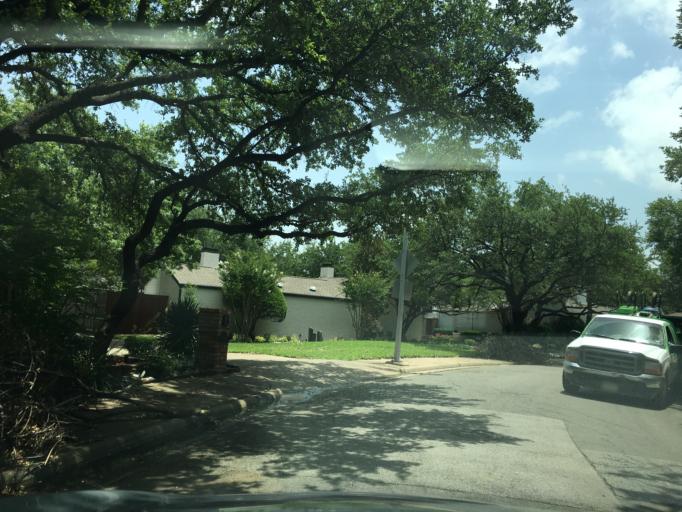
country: US
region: Texas
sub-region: Dallas County
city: University Park
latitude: 32.9075
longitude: -96.7916
